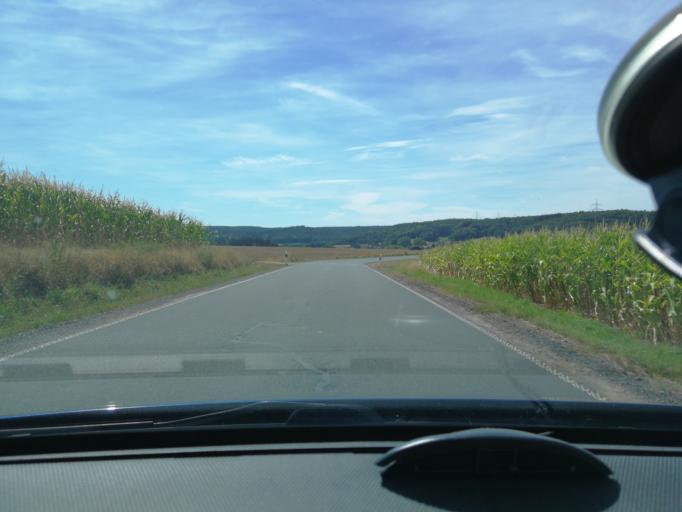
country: DE
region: Rheinland-Pfalz
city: Heidweiler
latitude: 49.9167
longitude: 6.7569
